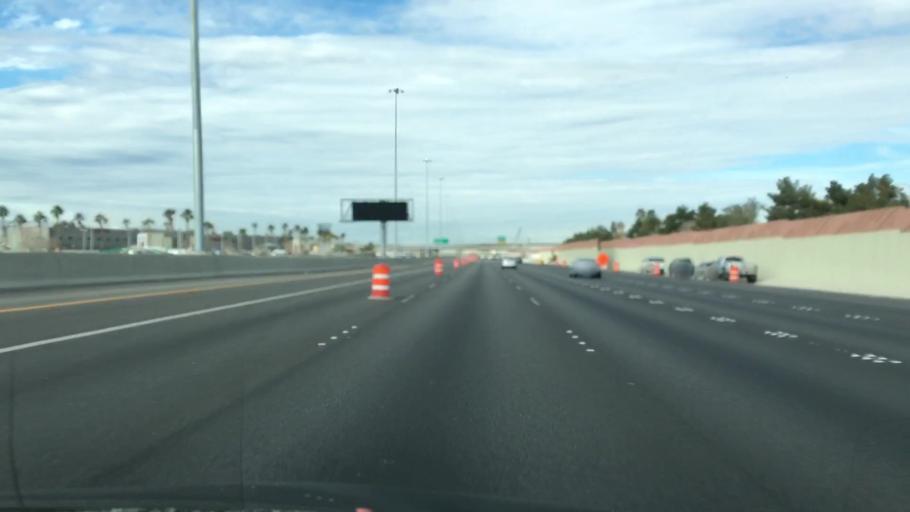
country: US
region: Nevada
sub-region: Clark County
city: Las Vegas
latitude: 36.2664
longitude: -115.2565
